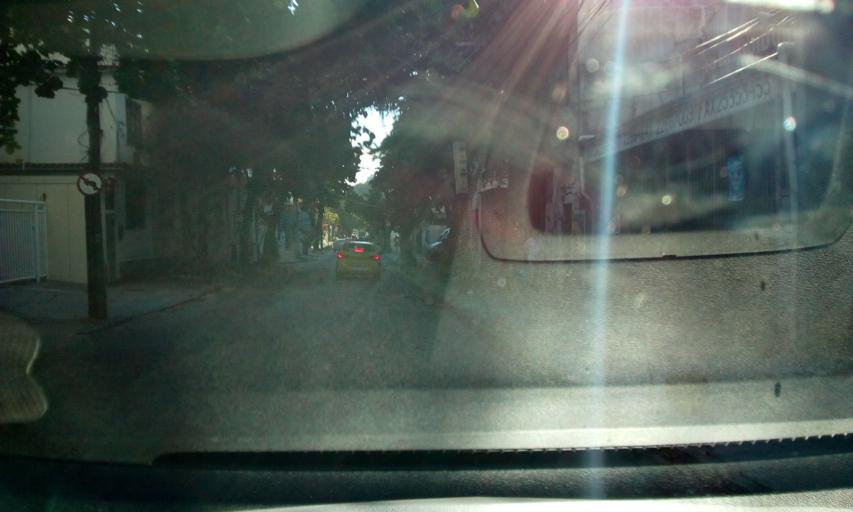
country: BR
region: Rio de Janeiro
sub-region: Rio De Janeiro
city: Rio de Janeiro
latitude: -22.9585
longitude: -43.1956
